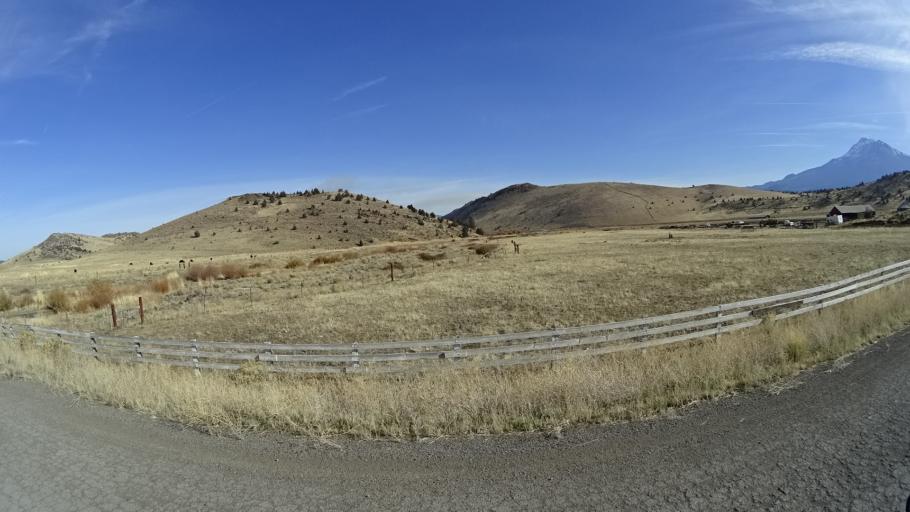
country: US
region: California
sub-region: Siskiyou County
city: Weed
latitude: 41.5035
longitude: -122.4561
